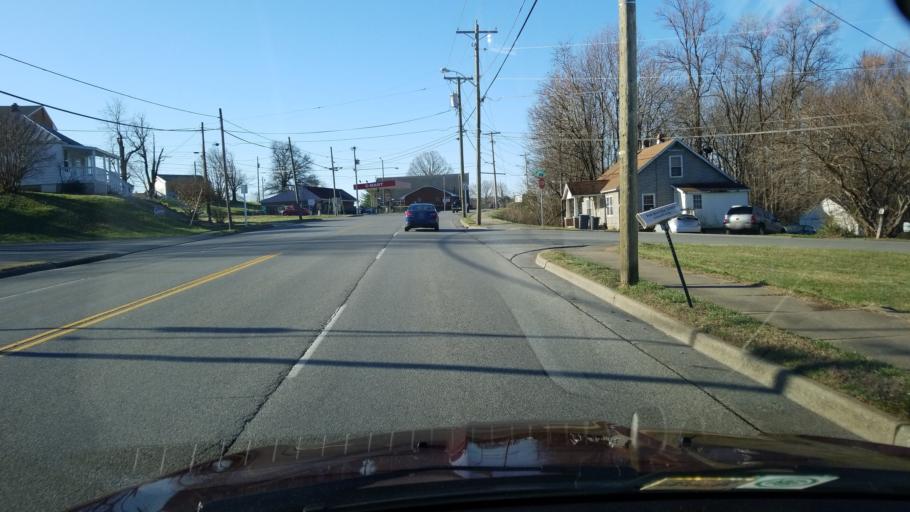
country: US
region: Virginia
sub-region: Franklin County
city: Rocky Mount
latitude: 37.0064
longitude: -79.8949
